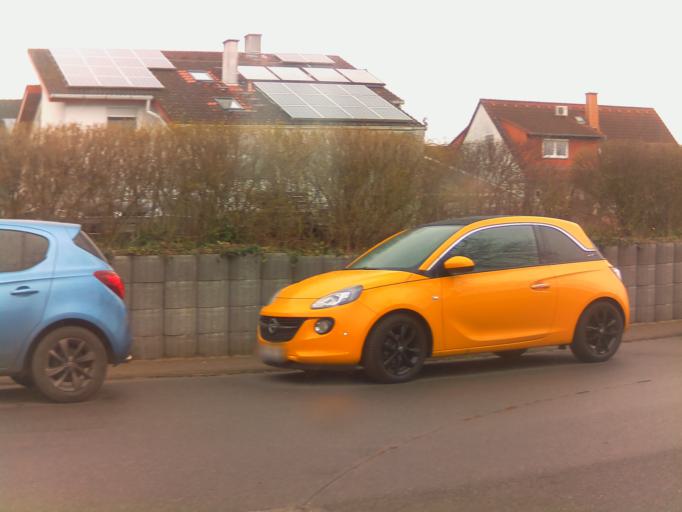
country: DE
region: Hesse
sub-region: Regierungsbezirk Darmstadt
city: Riedstadt
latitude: 49.8321
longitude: 8.4749
